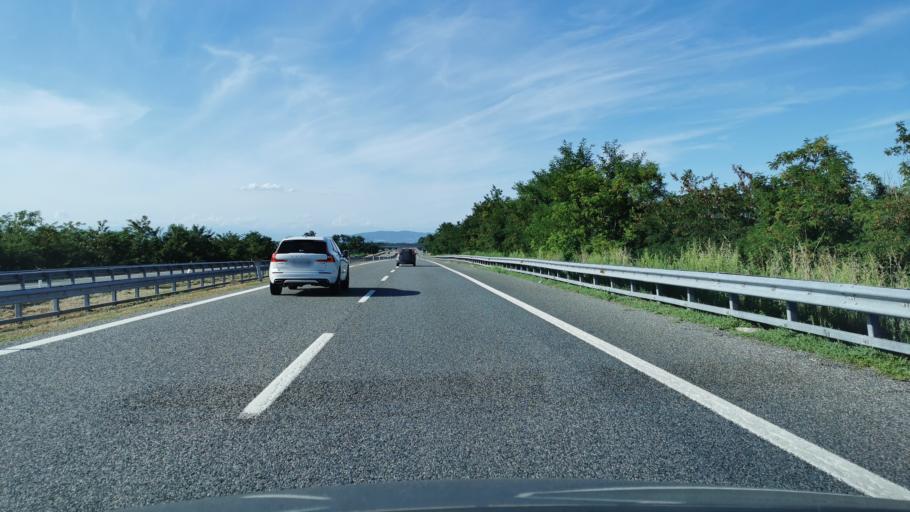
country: IT
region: Piedmont
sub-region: Provincia di Cuneo
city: Caramagna Piemonte
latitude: 44.8092
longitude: 7.7520
